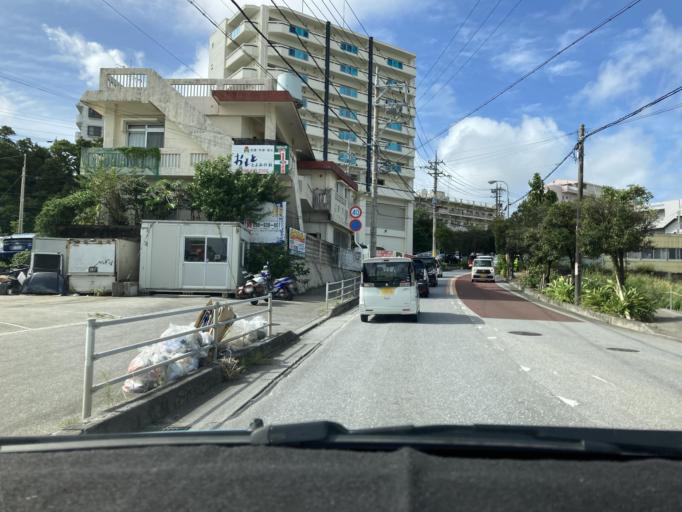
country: JP
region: Okinawa
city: Tomigusuku
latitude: 26.1776
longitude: 127.6843
